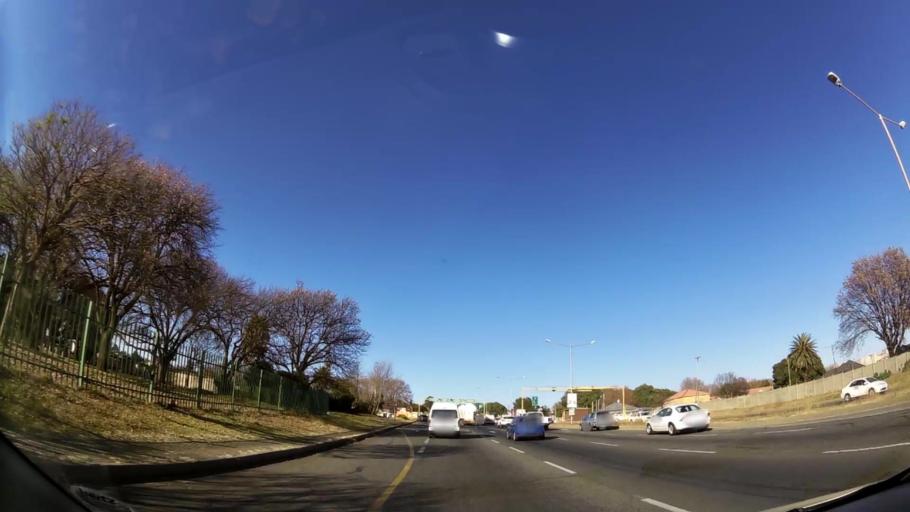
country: ZA
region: Gauteng
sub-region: West Rand District Municipality
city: Krugersdorp
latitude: -26.1036
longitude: 27.7791
